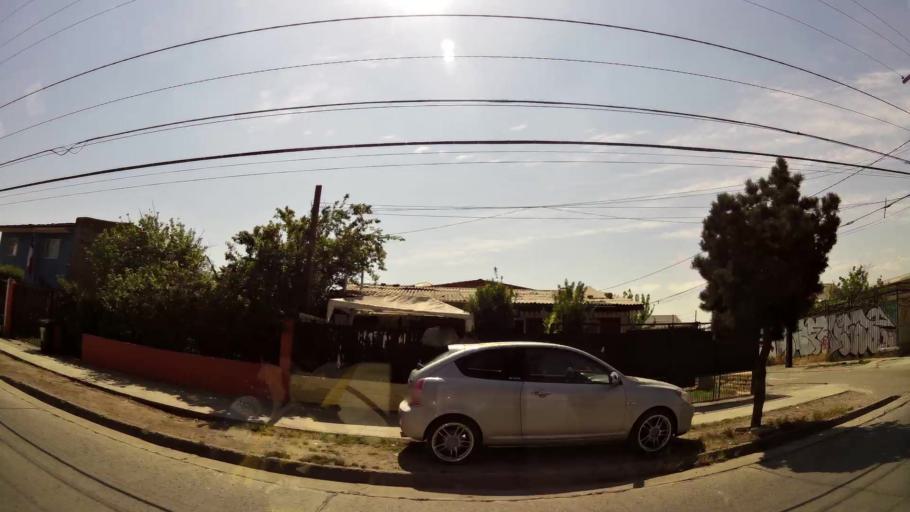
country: CL
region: Santiago Metropolitan
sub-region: Provincia de Santiago
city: La Pintana
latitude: -33.5463
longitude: -70.6421
